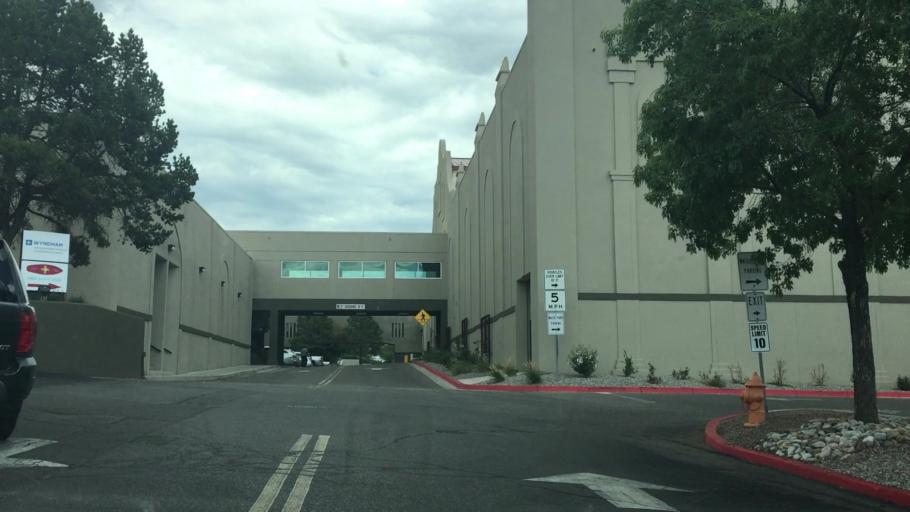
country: US
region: New Mexico
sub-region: Bernalillo County
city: Albuquerque
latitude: 35.1074
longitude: -106.6039
